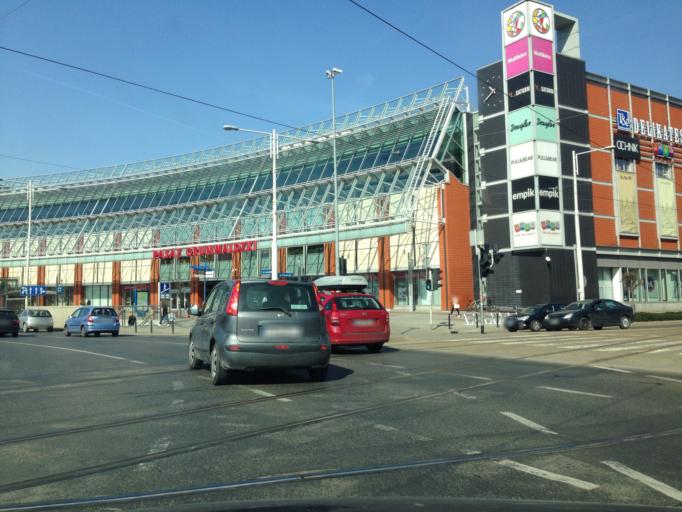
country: PL
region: Lower Silesian Voivodeship
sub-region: Powiat wroclawski
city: Wroclaw
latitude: 51.1119
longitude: 17.0610
